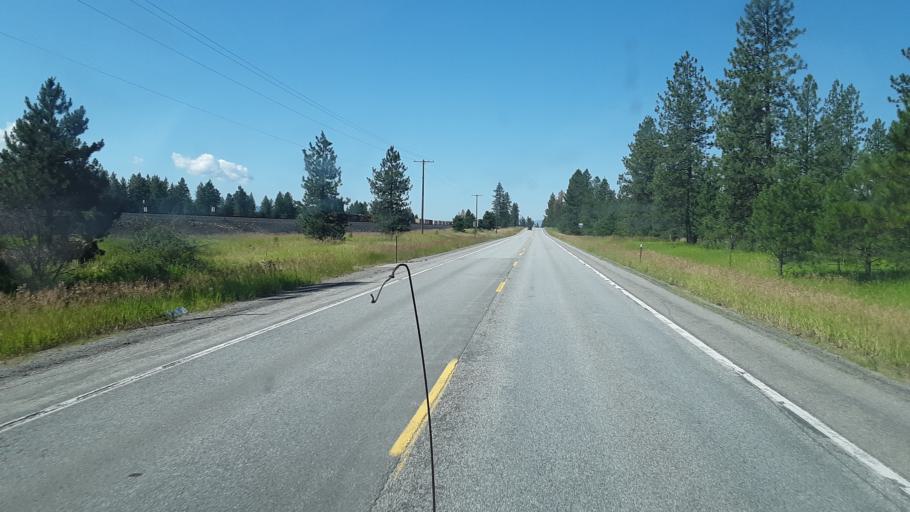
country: US
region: Idaho
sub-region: Kootenai County
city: Rathdrum
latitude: 47.7983
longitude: -116.9214
